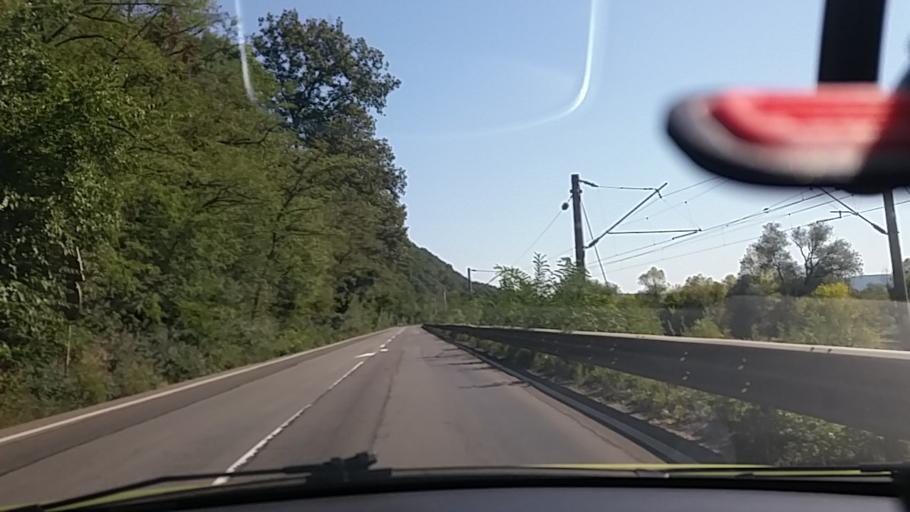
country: RO
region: Arad
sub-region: Comuna Conop
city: Conop
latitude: 46.0991
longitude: 21.8817
